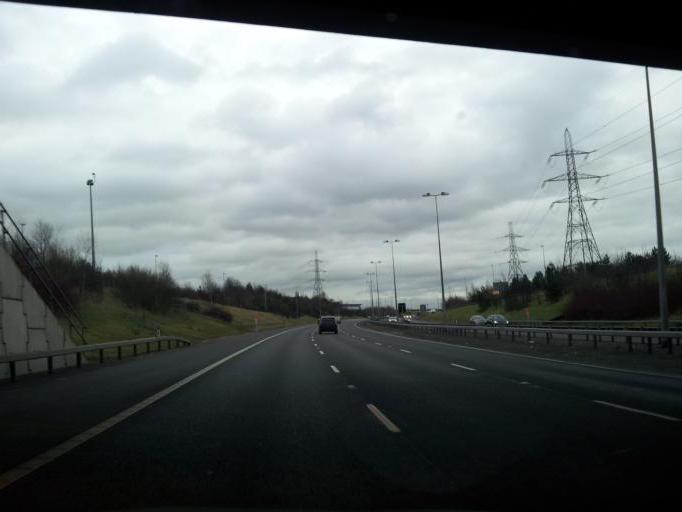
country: GB
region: England
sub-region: Staffordshire
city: Great Wyrley
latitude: 52.6726
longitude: -2.0193
